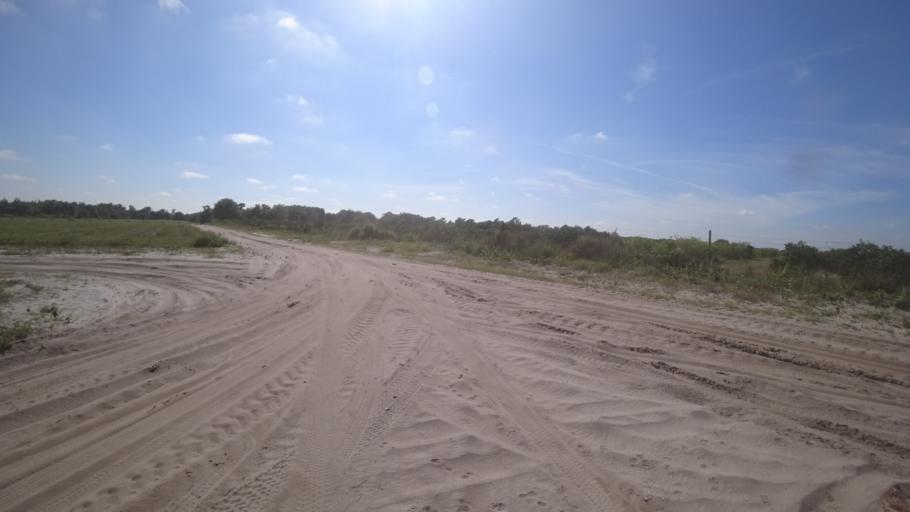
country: US
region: Florida
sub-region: DeSoto County
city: Arcadia
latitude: 27.2966
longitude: -82.0517
